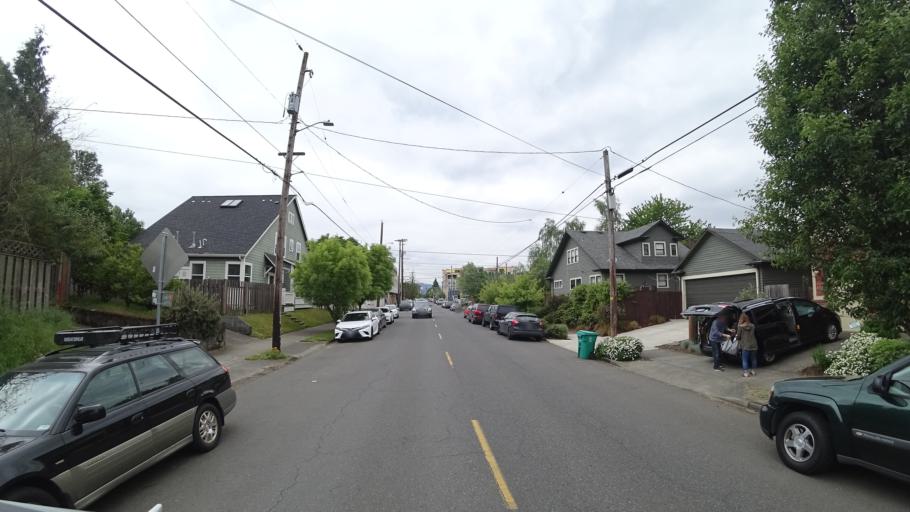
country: US
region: Oregon
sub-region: Multnomah County
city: Portland
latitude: 45.5520
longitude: -122.6651
